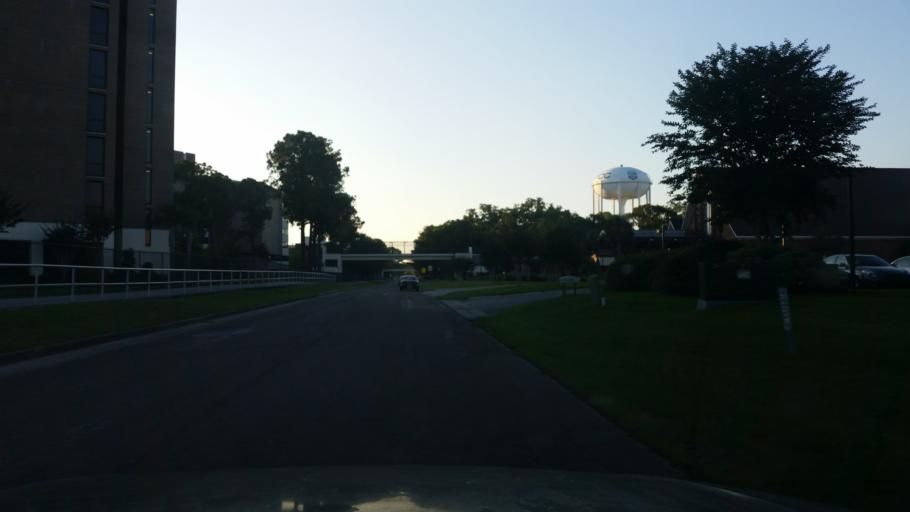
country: US
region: Florida
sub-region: Escambia County
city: Brent
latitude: 30.4732
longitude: -87.2311
